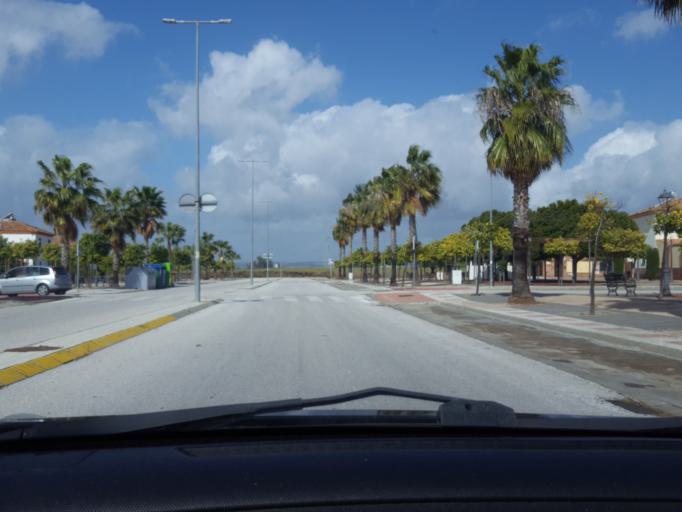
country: ES
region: Andalusia
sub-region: Provincia de Sevilla
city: Acala del Rio
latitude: 37.5142
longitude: -5.9879
